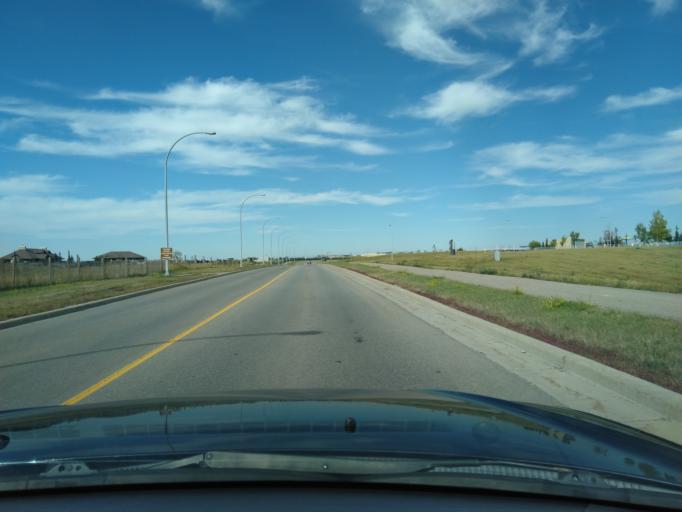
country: CA
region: Alberta
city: Calgary
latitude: 51.0972
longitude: -113.9875
